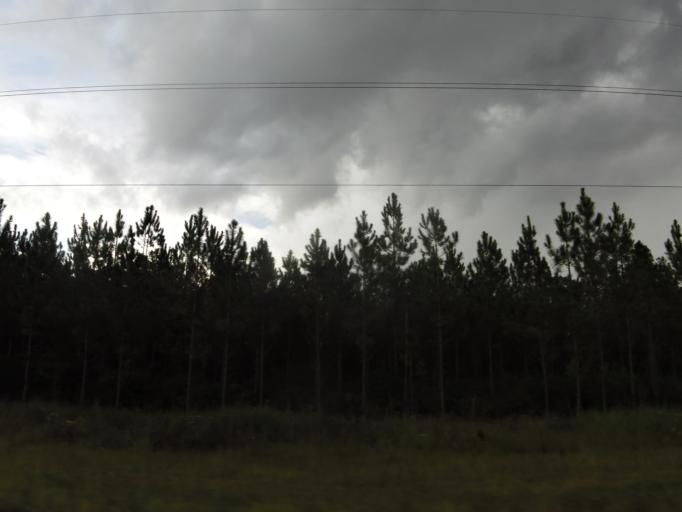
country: US
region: Florida
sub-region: Nassau County
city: Hilliard
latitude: 30.5675
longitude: -82.0441
